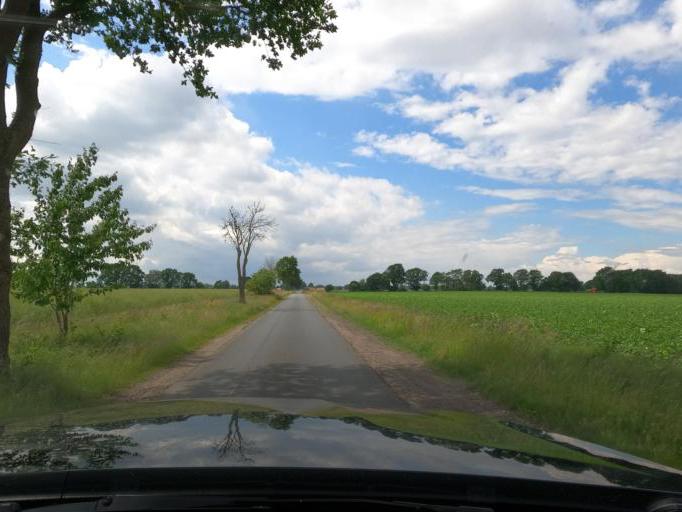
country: DE
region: Lower Saxony
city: Steimbke
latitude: 52.6293
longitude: 9.4121
